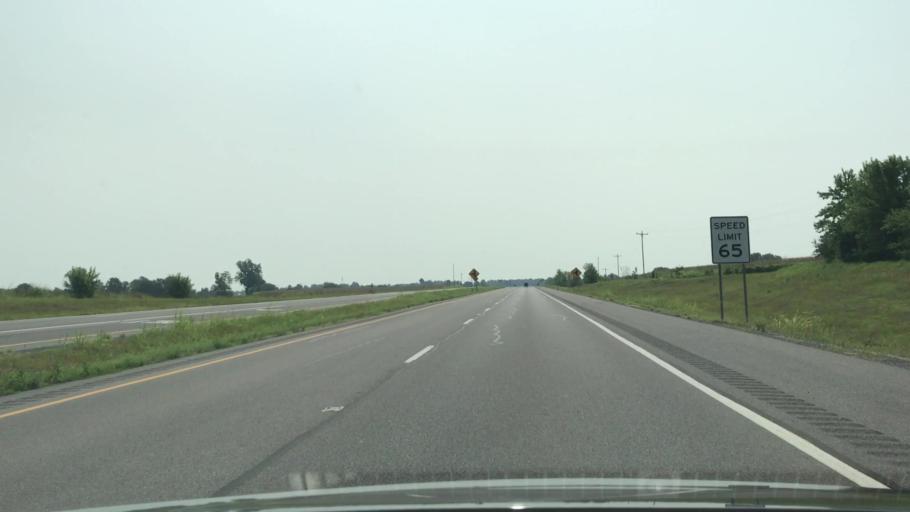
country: US
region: Kentucky
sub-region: Graves County
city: Mayfield
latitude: 36.6858
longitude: -88.5421
